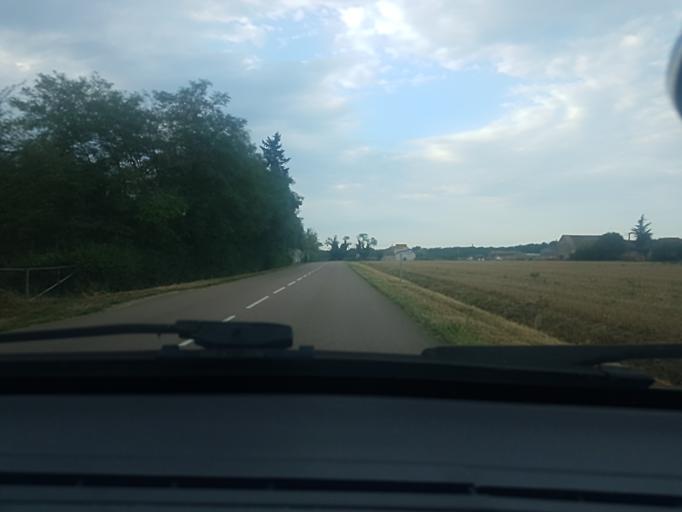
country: FR
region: Bourgogne
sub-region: Departement de Saone-et-Loire
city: Buxy
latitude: 46.7311
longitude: 4.7493
